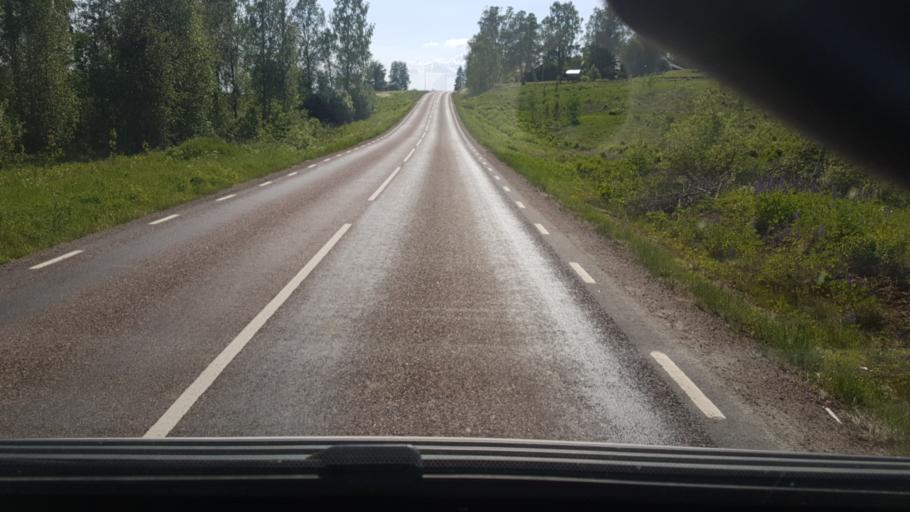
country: SE
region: Vaermland
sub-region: Eda Kommun
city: Charlottenberg
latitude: 59.8877
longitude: 12.3336
